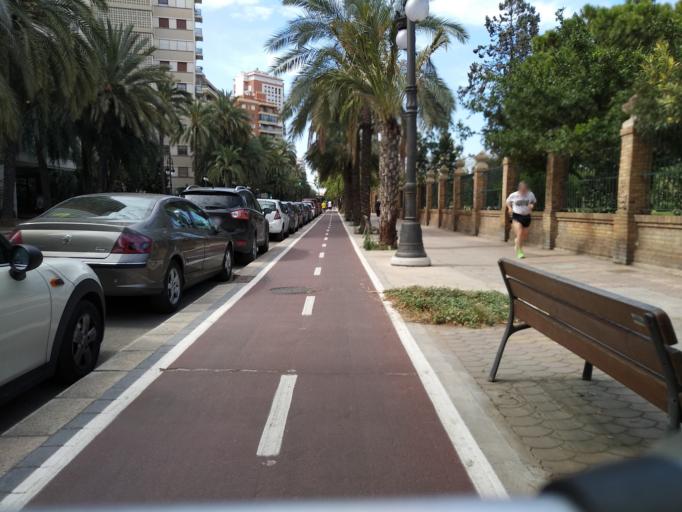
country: ES
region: Valencia
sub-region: Provincia de Valencia
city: Tavernes Blanques
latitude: 39.4828
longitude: -0.3648
